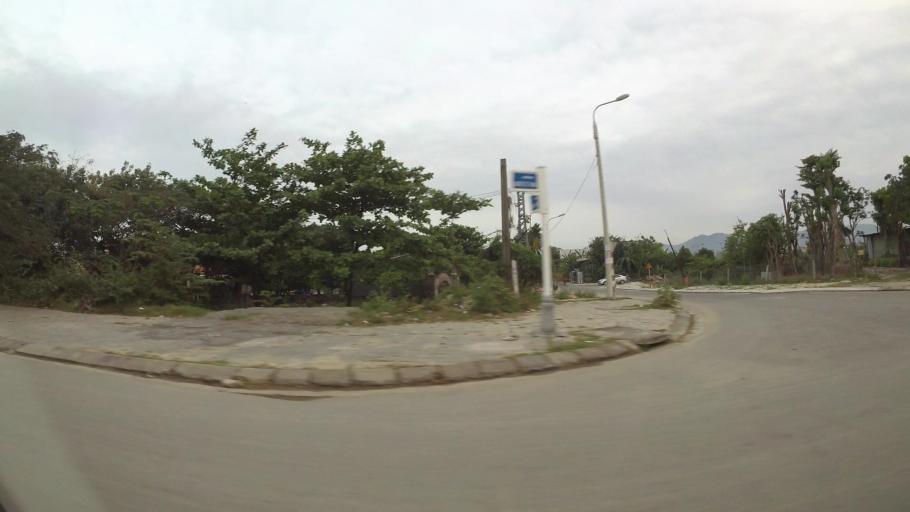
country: VN
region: Da Nang
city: Lien Chieu
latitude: 16.1081
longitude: 108.1285
